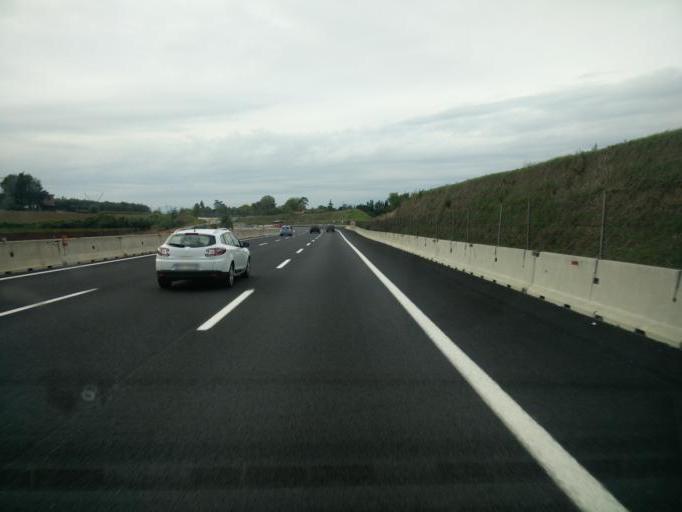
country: IT
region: Tuscany
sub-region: Province of Florence
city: Scandicci
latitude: 43.7419
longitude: 11.1817
